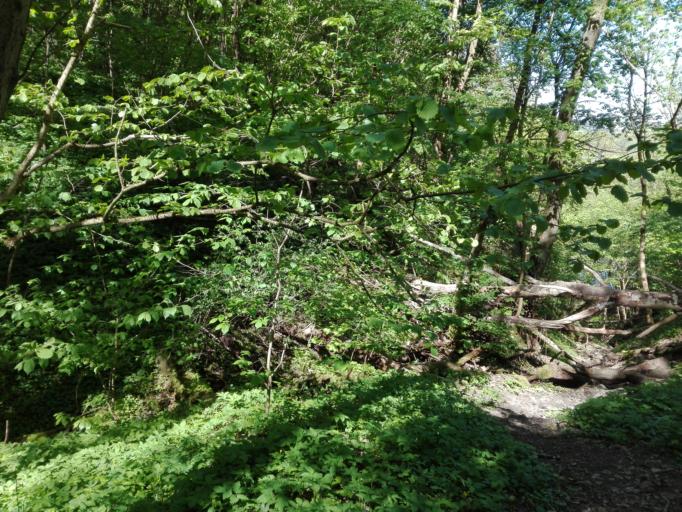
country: LT
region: Vilnius County
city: Lazdynai
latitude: 54.6856
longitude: 25.2224
